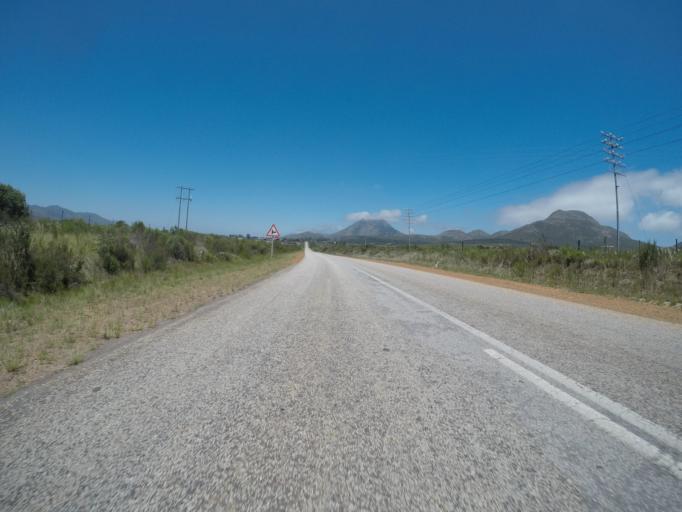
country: ZA
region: Eastern Cape
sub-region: Cacadu District Municipality
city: Kareedouw
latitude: -33.9423
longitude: 24.2676
